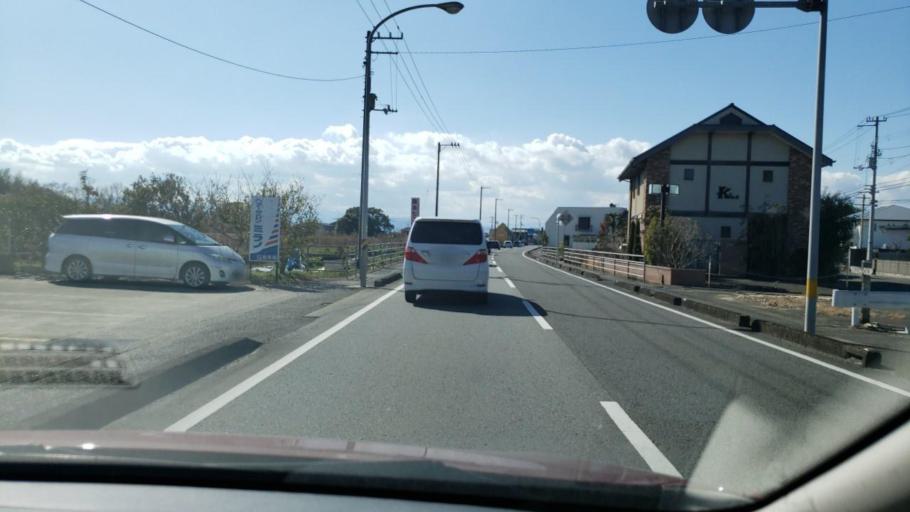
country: JP
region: Tokushima
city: Narutocho-mitsuishi
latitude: 34.1572
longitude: 134.5342
